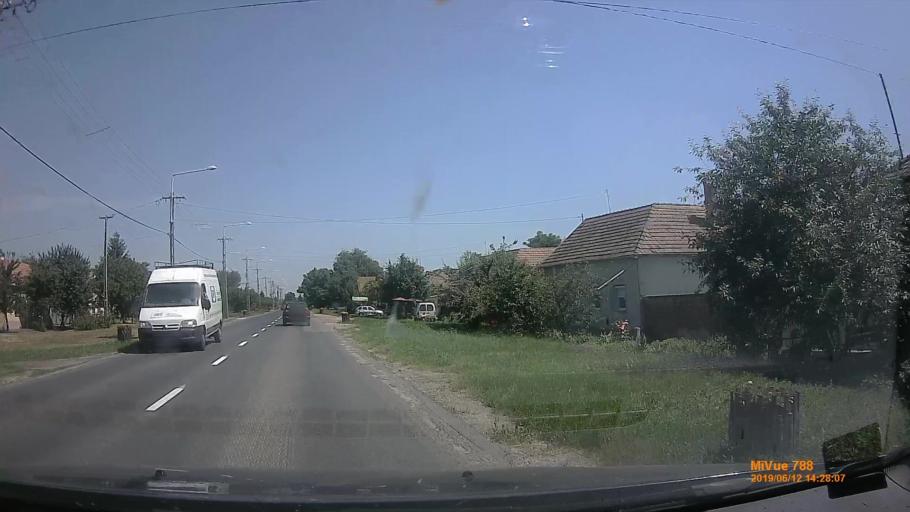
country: HU
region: Csongrad
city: Maroslele
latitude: 46.2143
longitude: 20.3604
